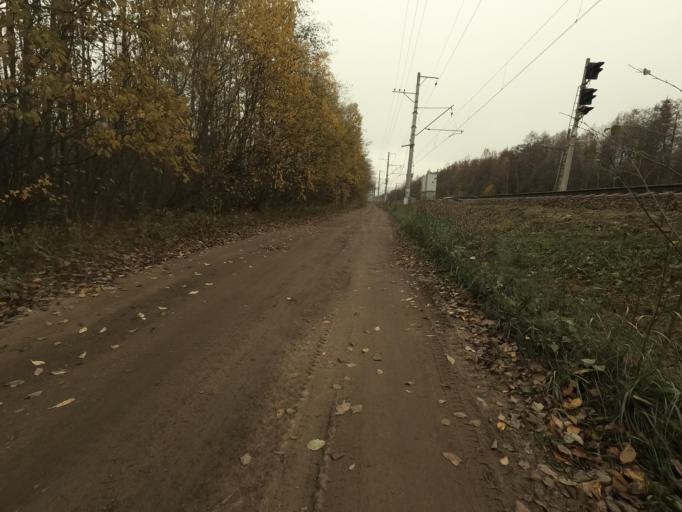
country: RU
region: Leningrad
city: Pavlovo
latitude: 59.7866
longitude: 30.8901
